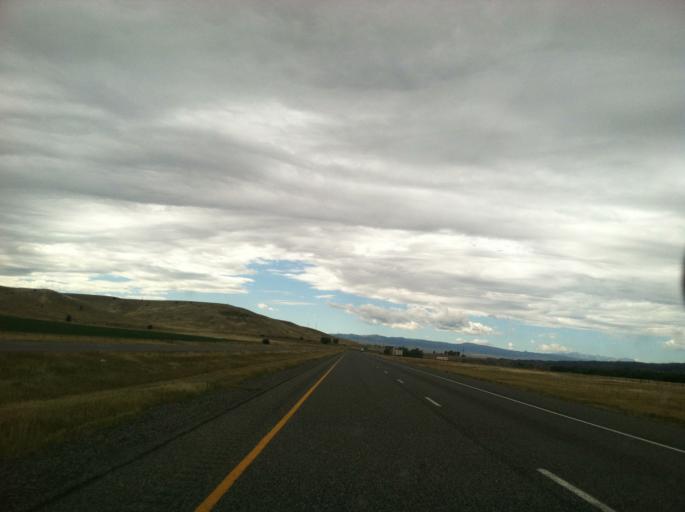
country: US
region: Montana
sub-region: Park County
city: Livingston
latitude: 45.7069
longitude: -110.3743
